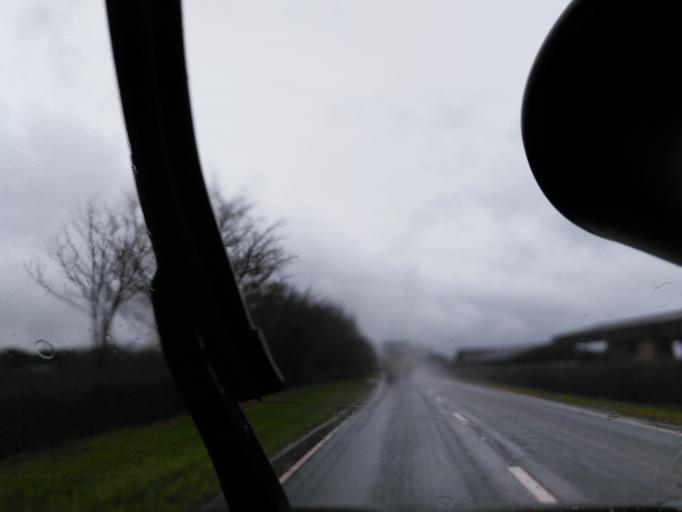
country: GB
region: England
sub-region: Somerset
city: Shepton Mallet
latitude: 51.1694
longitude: -2.5603
